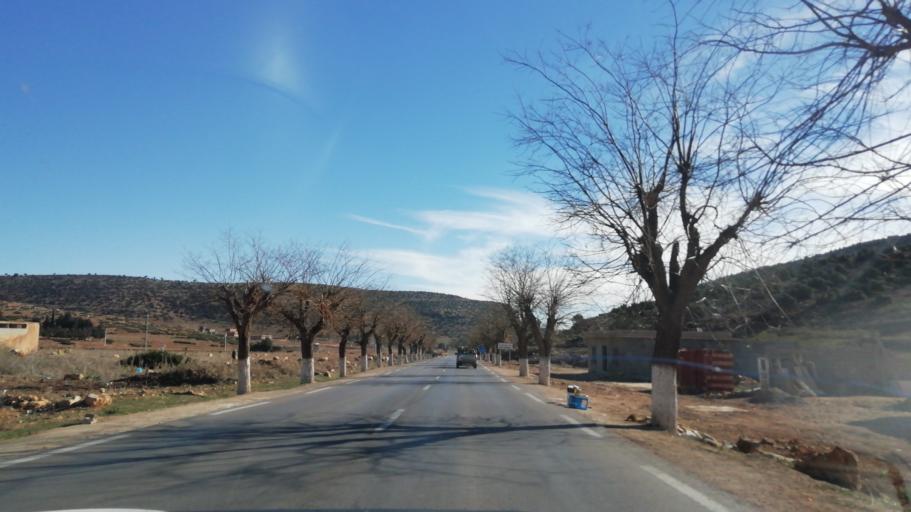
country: DZ
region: Tlemcen
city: Sebdou
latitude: 34.7037
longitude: -1.3171
